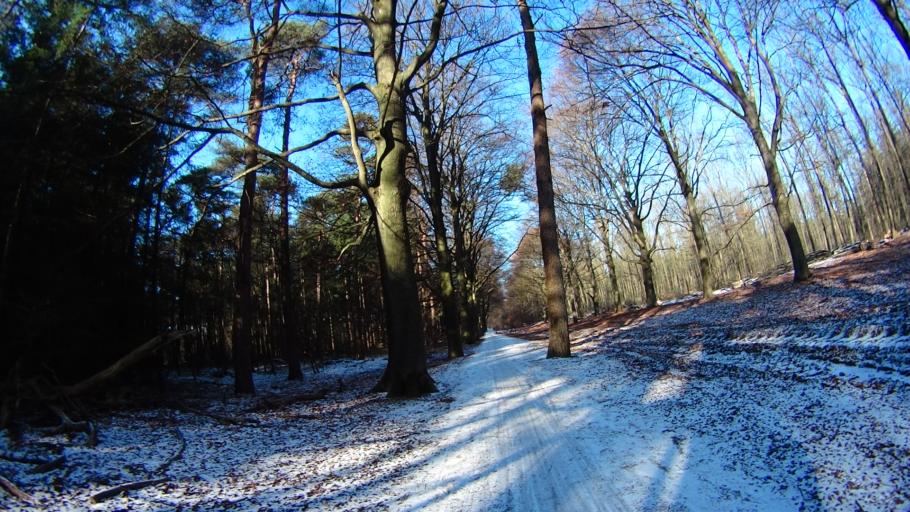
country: NL
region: North Holland
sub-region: Gemeente Hilversum
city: Hilversum
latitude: 52.1865
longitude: 5.2182
